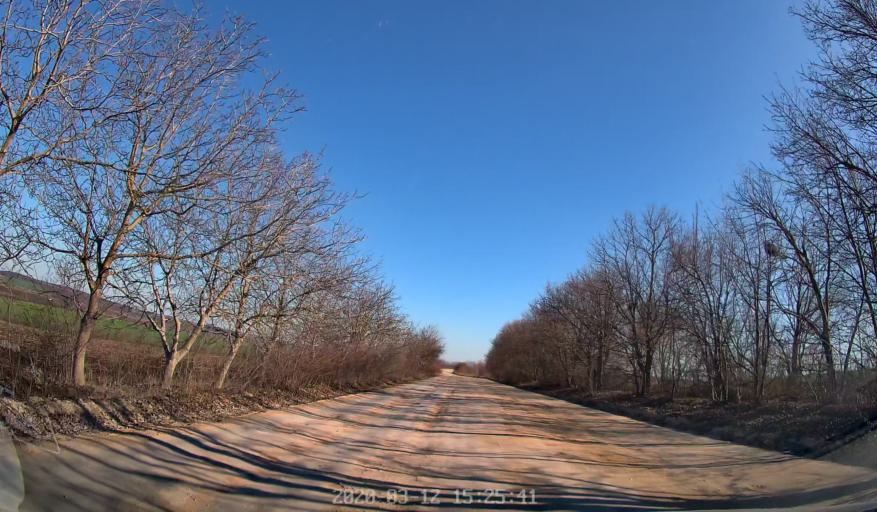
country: MD
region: Chisinau
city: Ciorescu
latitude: 47.1815
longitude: 28.9199
